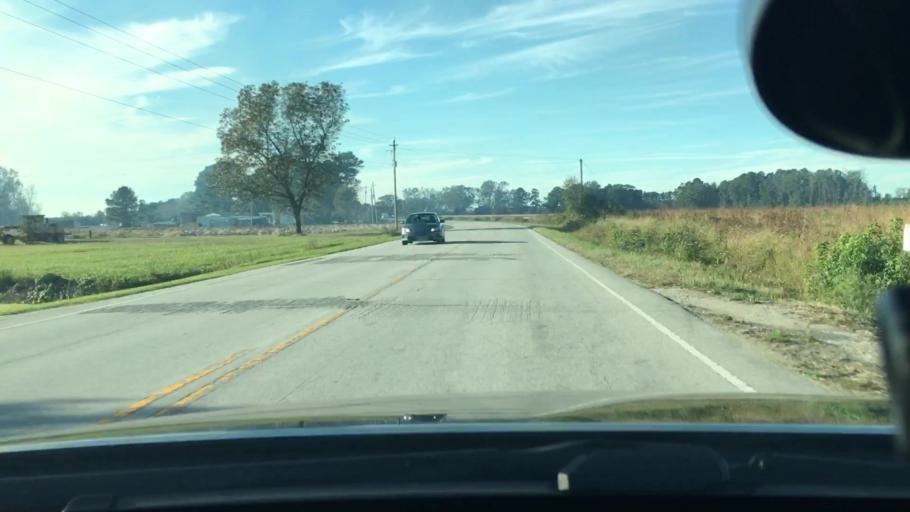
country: US
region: North Carolina
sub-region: Craven County
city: Vanceboro
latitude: 35.3719
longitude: -77.2081
